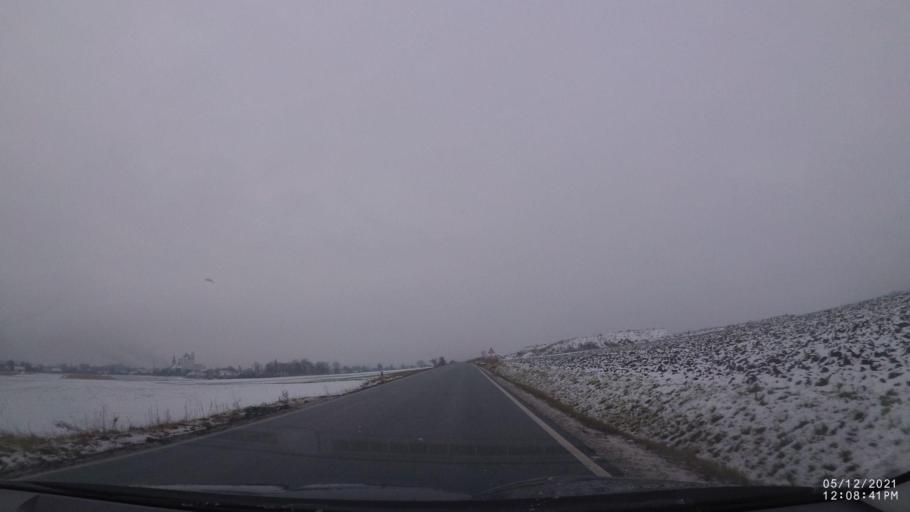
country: CZ
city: Ceske Mezirici
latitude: 50.2876
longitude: 16.0315
